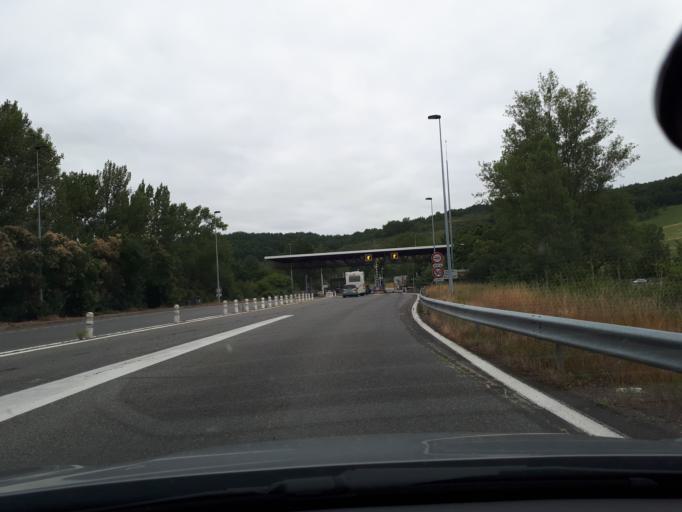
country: FR
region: Midi-Pyrenees
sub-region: Departement du Tarn-et-Garonne
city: Auvillar
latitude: 44.0638
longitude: 0.8653
